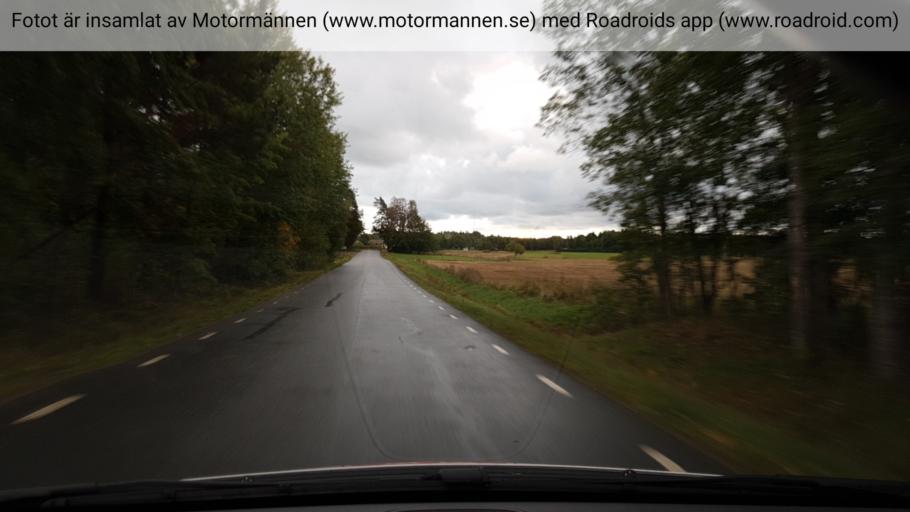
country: SE
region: Vaermland
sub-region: Saffle Kommun
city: Saeffle
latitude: 58.9366
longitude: 13.1761
